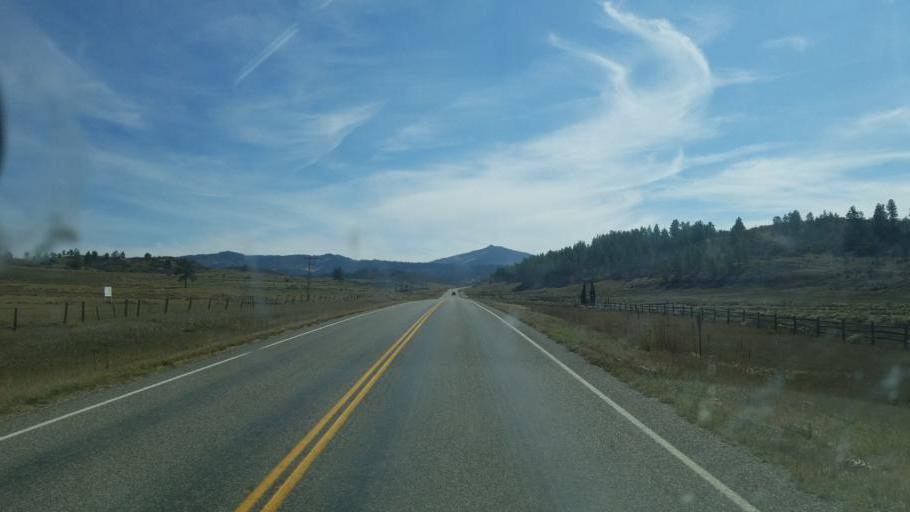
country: US
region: New Mexico
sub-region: Rio Arriba County
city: Dulce
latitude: 37.0210
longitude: -106.8164
